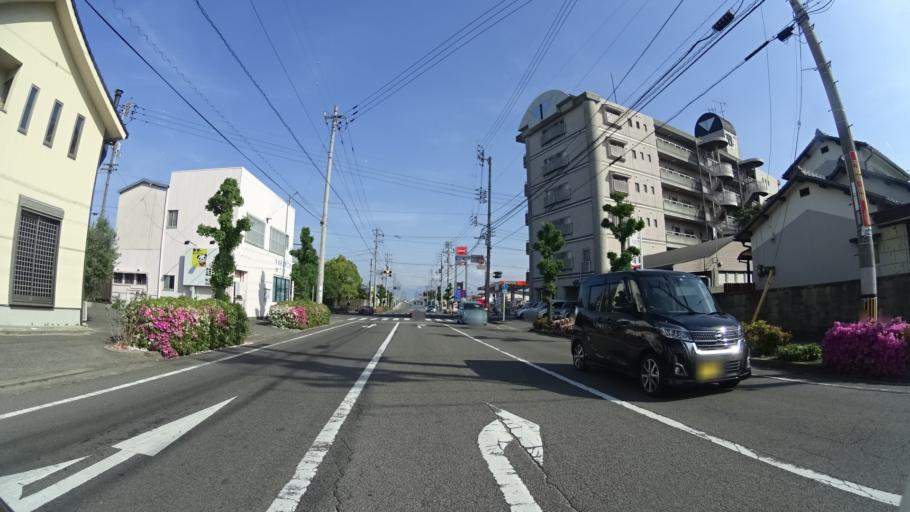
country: JP
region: Ehime
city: Saijo
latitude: 34.0611
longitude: 133.0112
